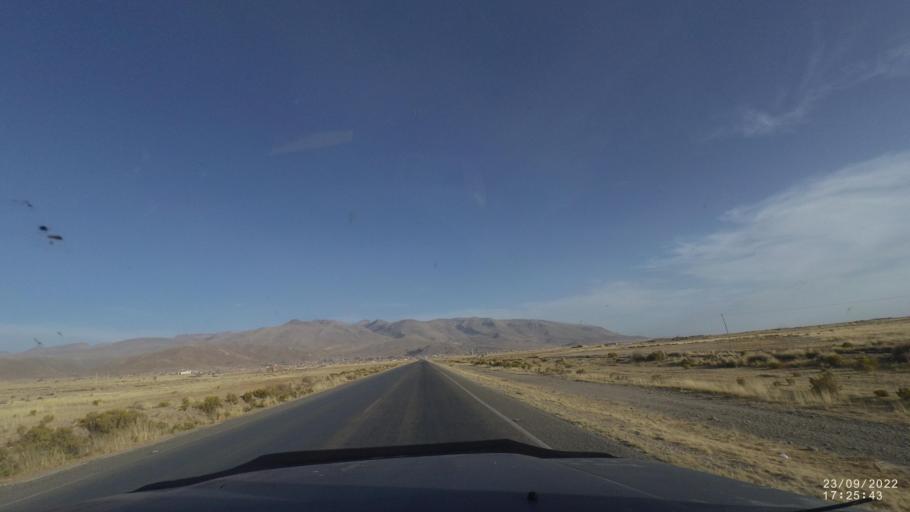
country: BO
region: Oruro
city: Challapata
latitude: -18.8747
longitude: -66.7941
